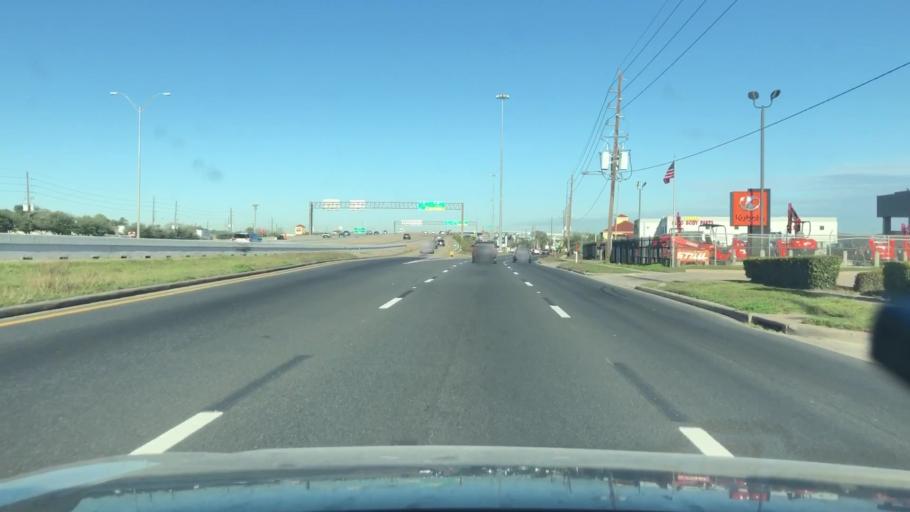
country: US
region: Texas
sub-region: Fort Bend County
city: Missouri City
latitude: 29.6513
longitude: -95.5471
